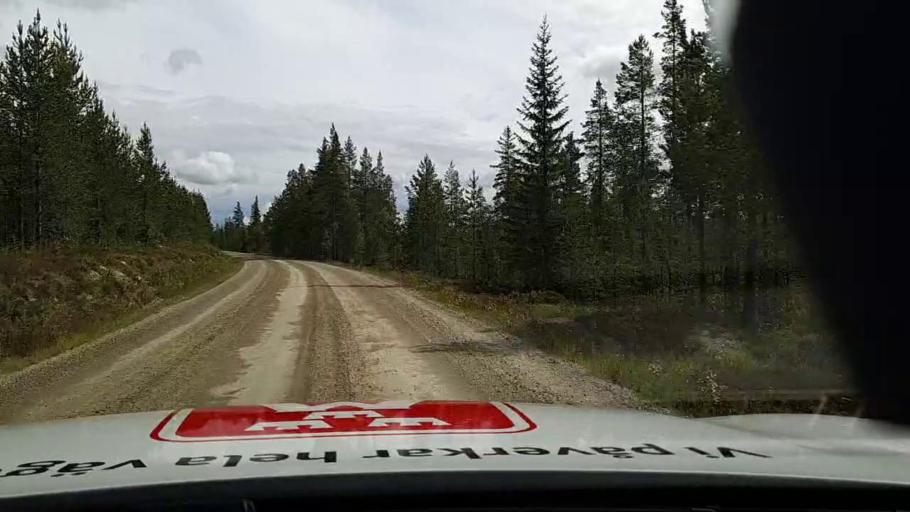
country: SE
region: Jaemtland
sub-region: Are Kommun
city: Jarpen
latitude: 62.5361
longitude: 13.4773
